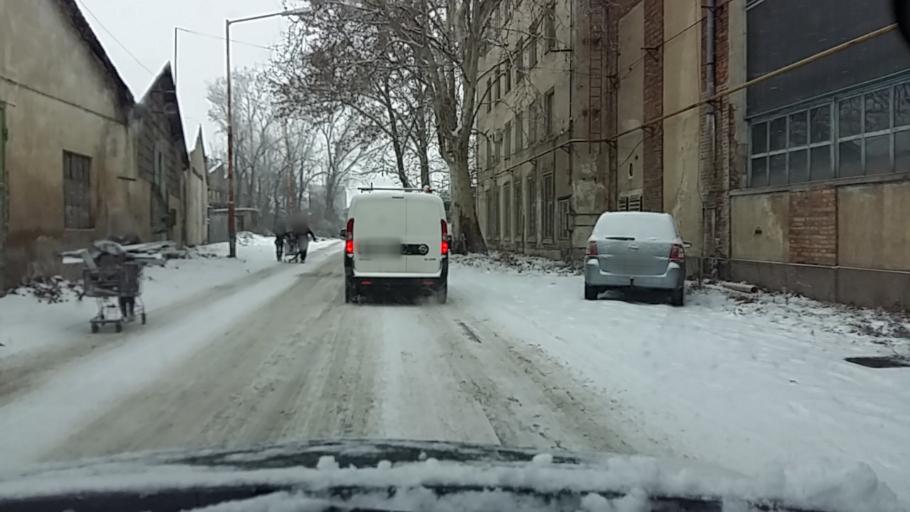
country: HU
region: Budapest
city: Budapest XXII. keruelet
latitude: 47.4237
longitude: 19.0540
